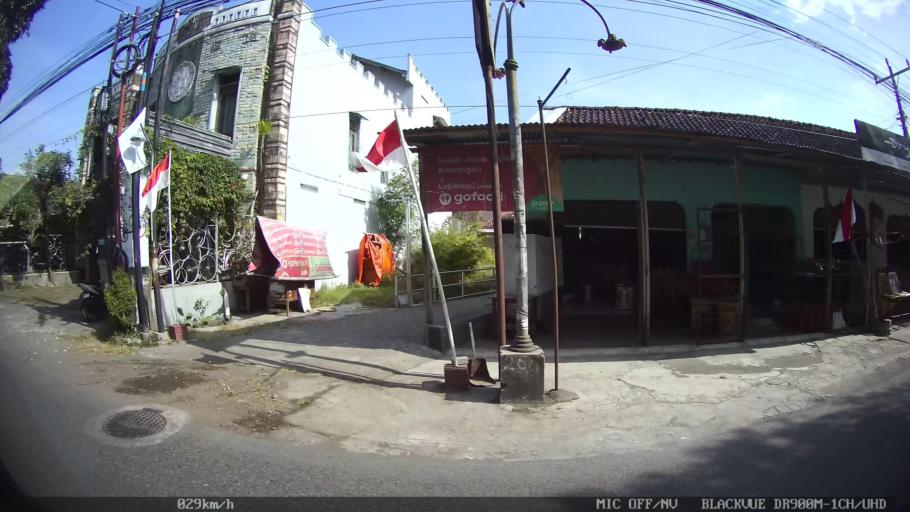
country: ID
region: Daerah Istimewa Yogyakarta
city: Kasihan
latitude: -7.8466
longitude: 110.3425
